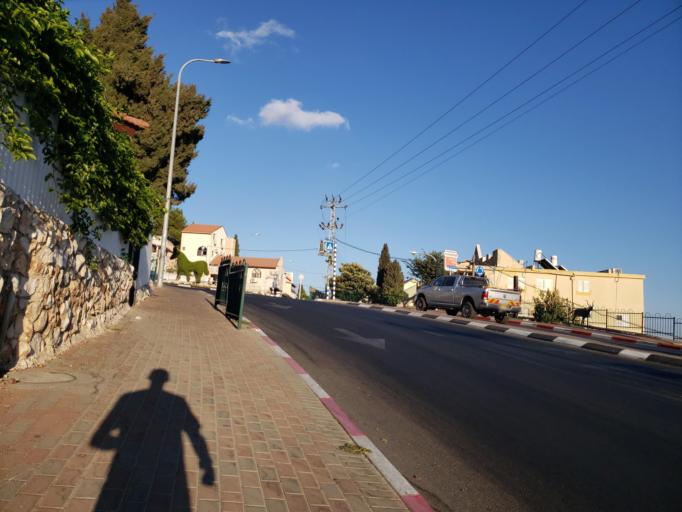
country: IL
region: Northern District
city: Safed
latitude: 32.9569
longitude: 35.4950
